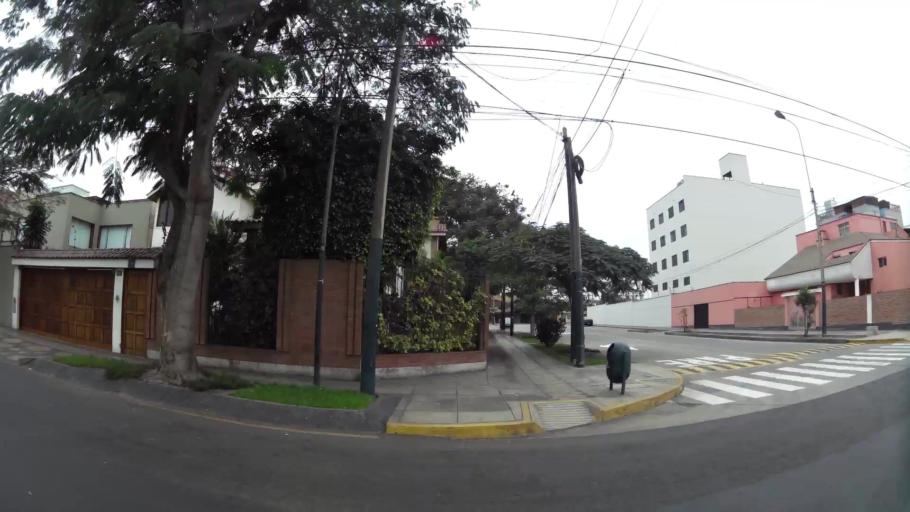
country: PE
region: Lima
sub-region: Lima
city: San Luis
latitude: -12.0943
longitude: -77.0142
